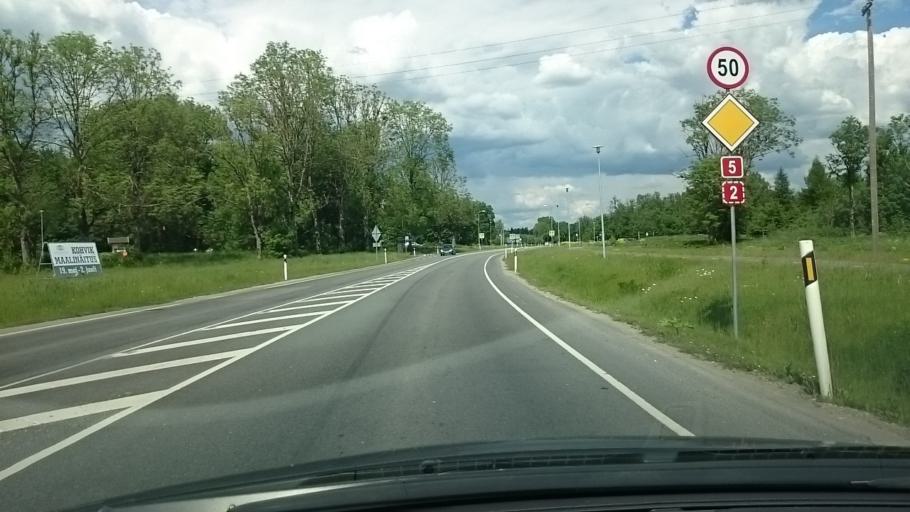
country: EE
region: Jaervamaa
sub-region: Tueri vald
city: Tueri
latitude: 58.8481
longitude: 25.4790
